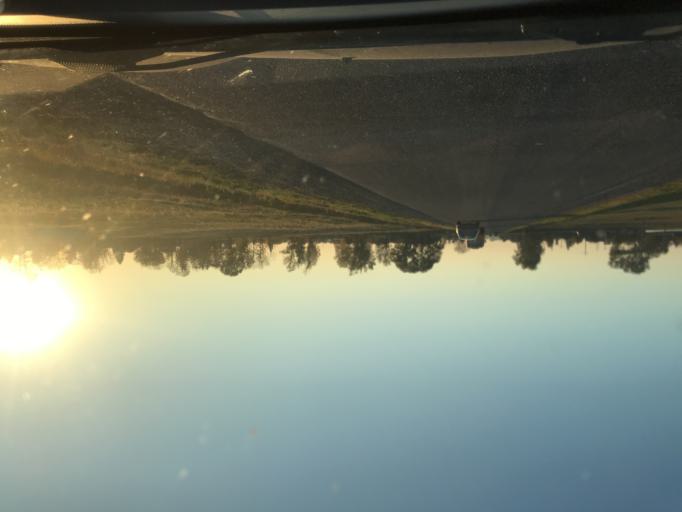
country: BY
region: Gomel
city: Brahin
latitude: 51.7976
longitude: 30.2633
